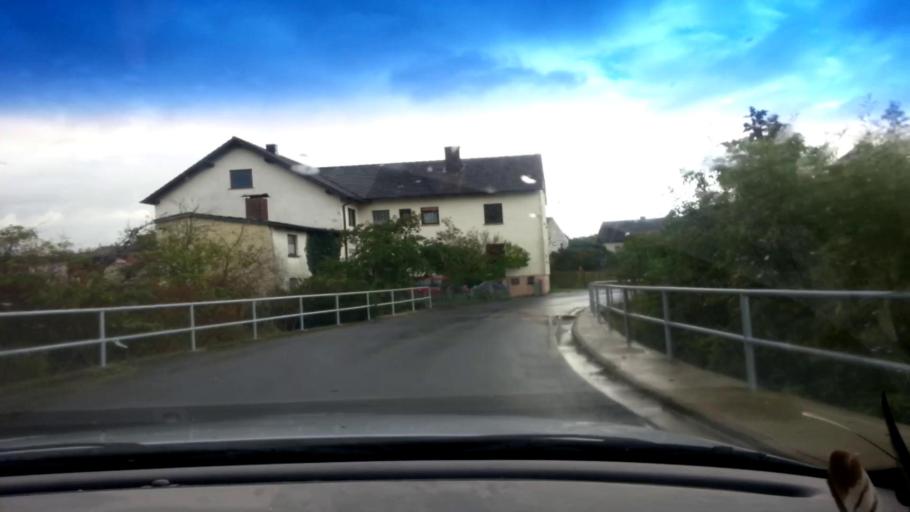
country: DE
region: Bavaria
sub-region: Upper Franconia
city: Burgebrach
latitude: 49.8257
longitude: 10.7066
